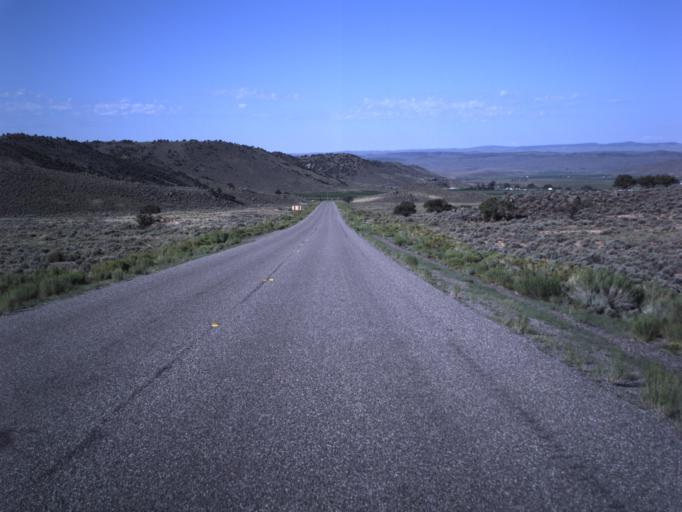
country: US
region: Utah
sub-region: Wayne County
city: Loa
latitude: 38.4752
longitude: -111.5717
